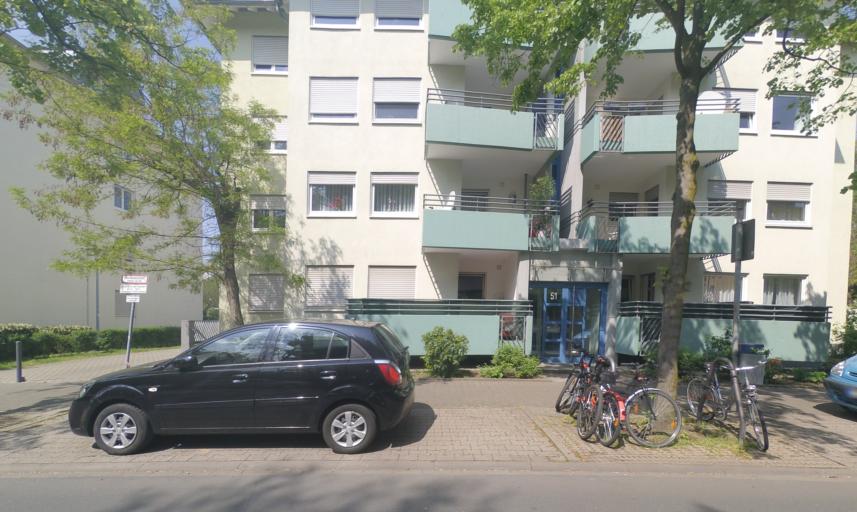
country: DE
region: Hesse
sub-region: Regierungsbezirk Darmstadt
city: Offenbach
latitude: 50.0891
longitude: 8.7523
